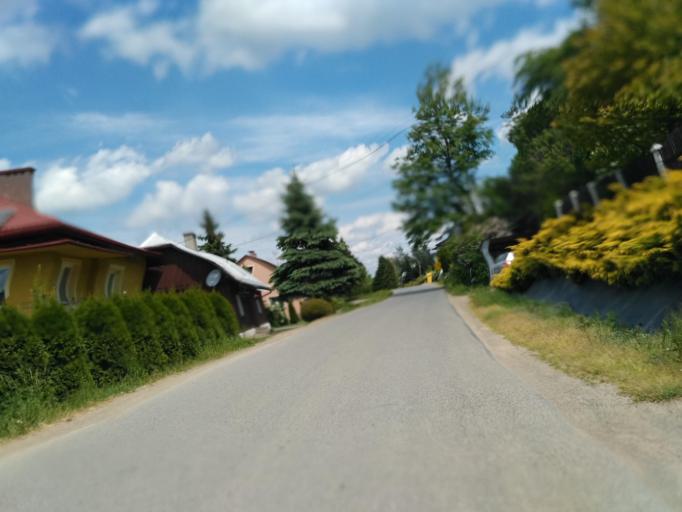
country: PL
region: Subcarpathian Voivodeship
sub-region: Powiat krosnienski
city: Dukla
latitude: 49.5699
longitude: 21.6158
